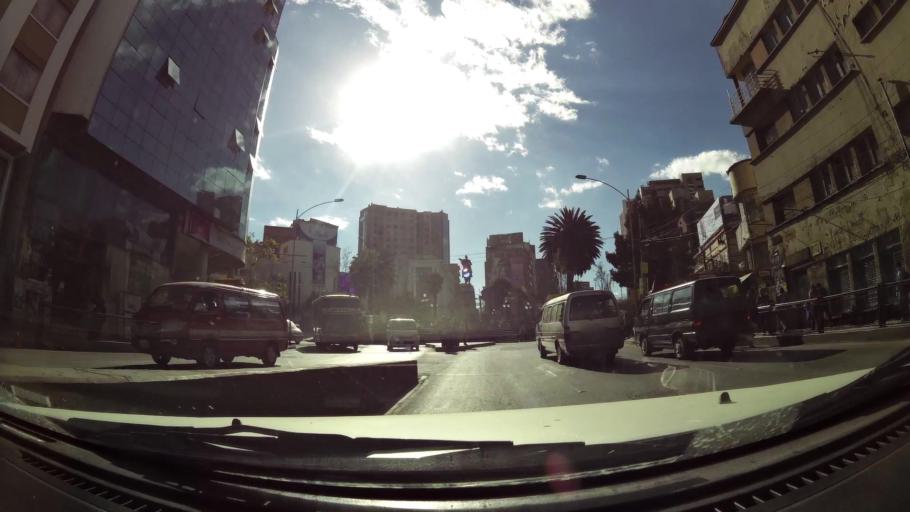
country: BO
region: La Paz
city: La Paz
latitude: -16.5046
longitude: -68.1307
